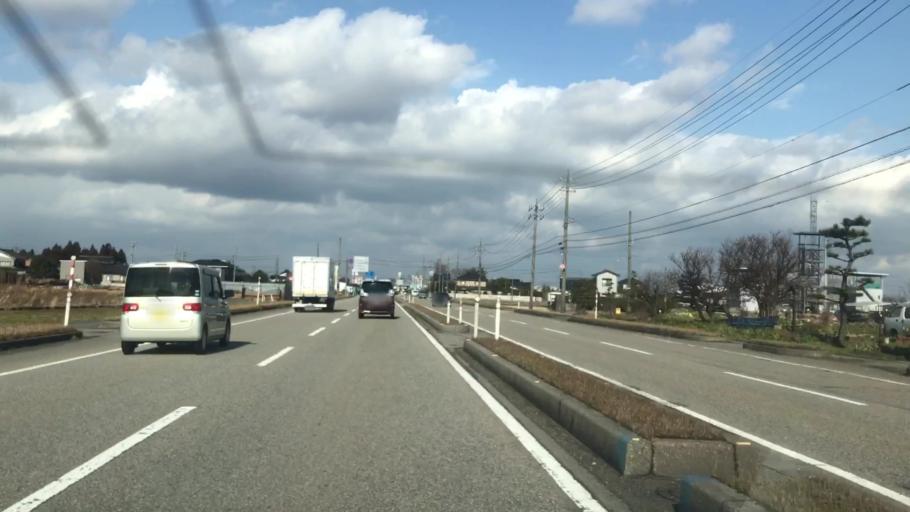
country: JP
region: Toyama
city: Kuragaki-kosugi
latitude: 36.7133
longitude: 137.0811
